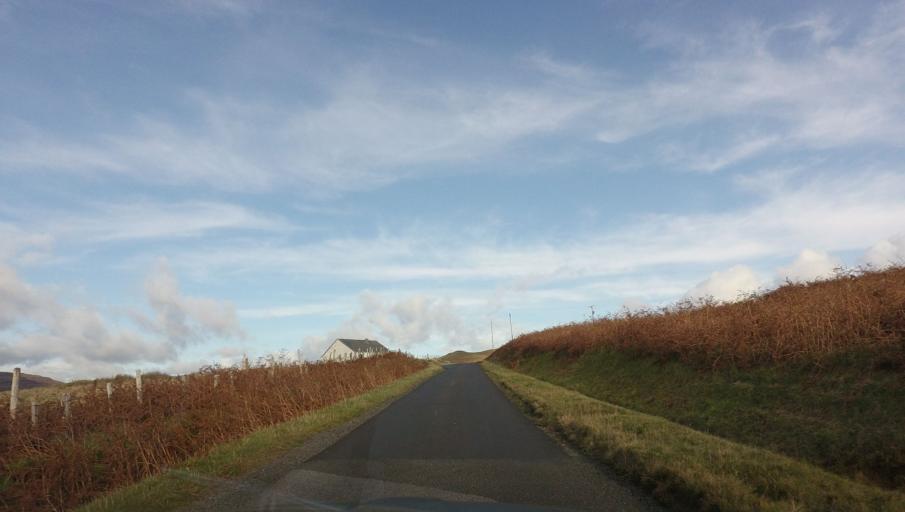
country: GB
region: Scotland
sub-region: Argyll and Bute
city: Isle Of Mull
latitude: 56.3217
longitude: -6.2147
